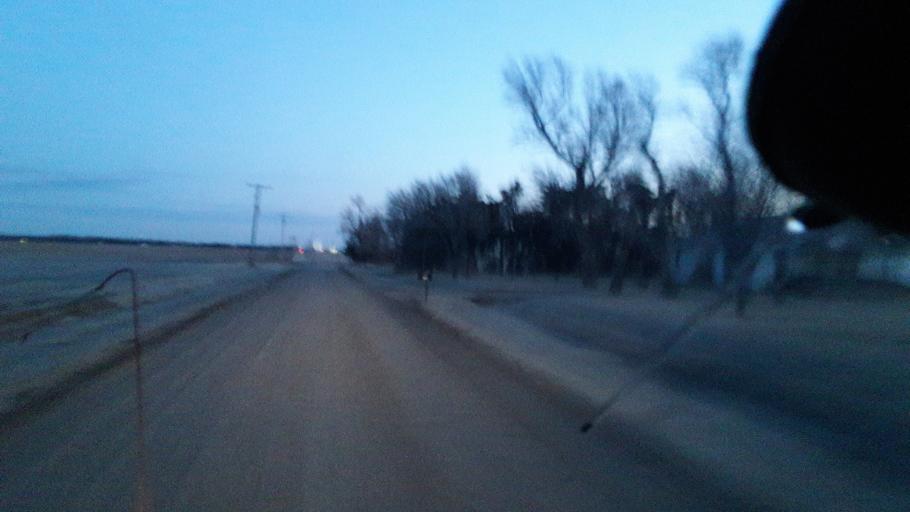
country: US
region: Kansas
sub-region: Reno County
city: South Hutchinson
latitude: 38.0043
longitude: -97.9769
